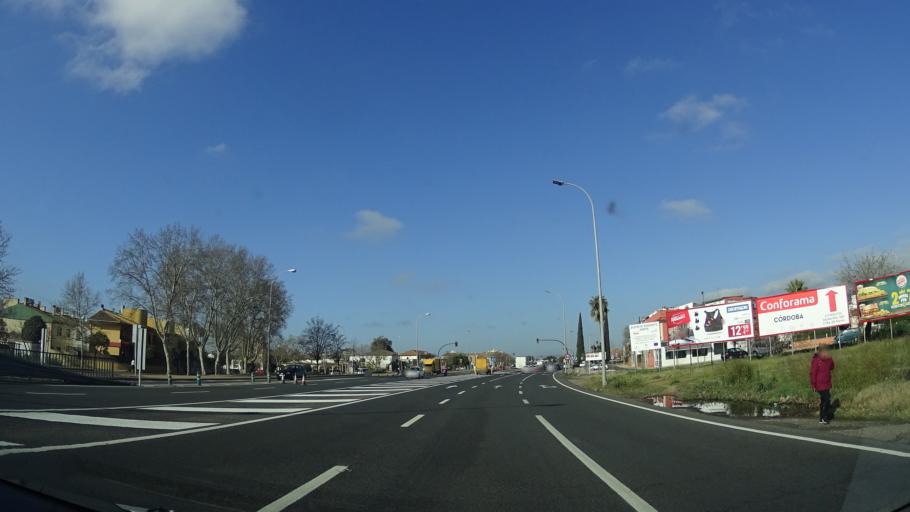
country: ES
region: Andalusia
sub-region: Province of Cordoba
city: Cordoba
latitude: 37.8824
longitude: -4.8080
